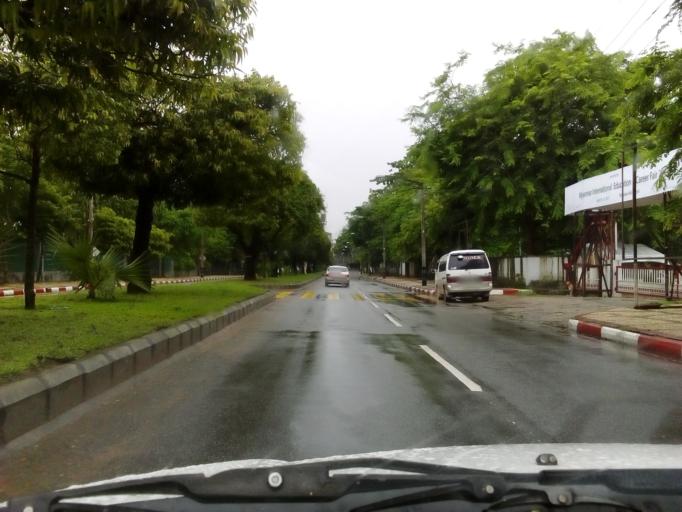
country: MM
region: Yangon
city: Yangon
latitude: 16.7851
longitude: 96.1512
